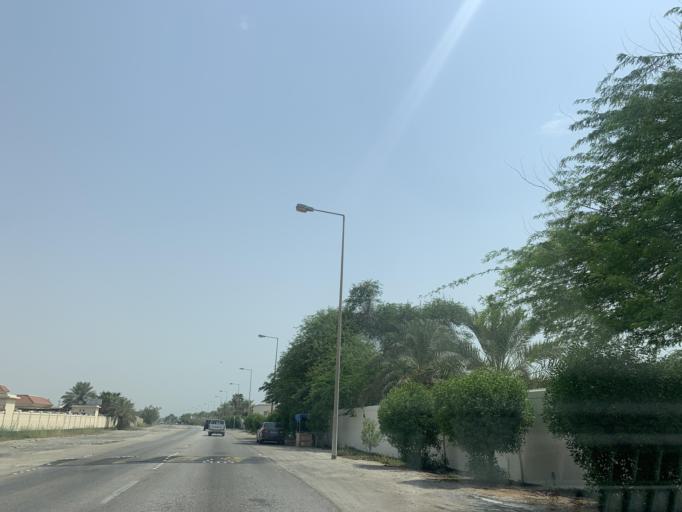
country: BH
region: Central Governorate
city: Madinat Hamad
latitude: 26.1656
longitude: 50.4653
